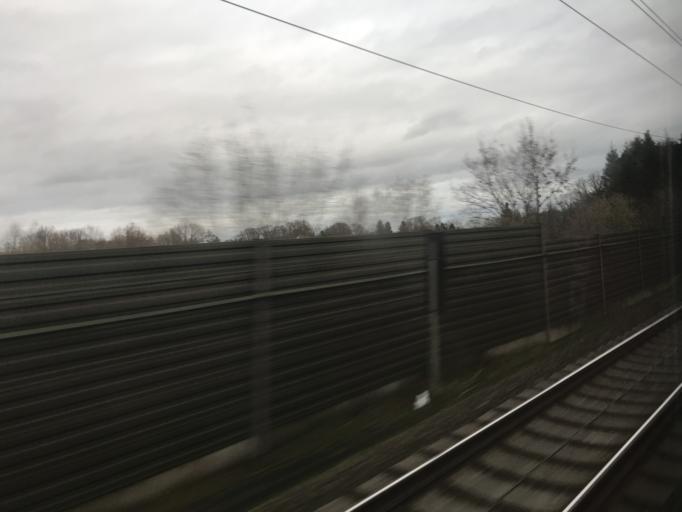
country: DE
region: Lower Saxony
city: Uetze
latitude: 52.4273
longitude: 10.2207
